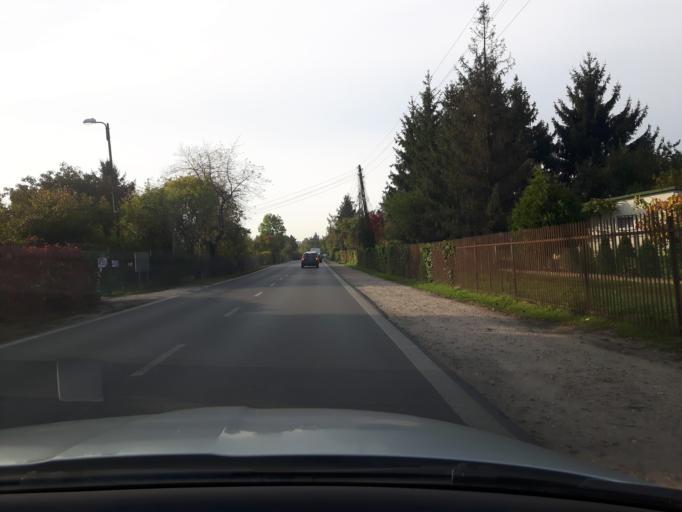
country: PL
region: Masovian Voivodeship
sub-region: Powiat wolominski
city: Zabki
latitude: 52.2824
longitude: 21.0964
